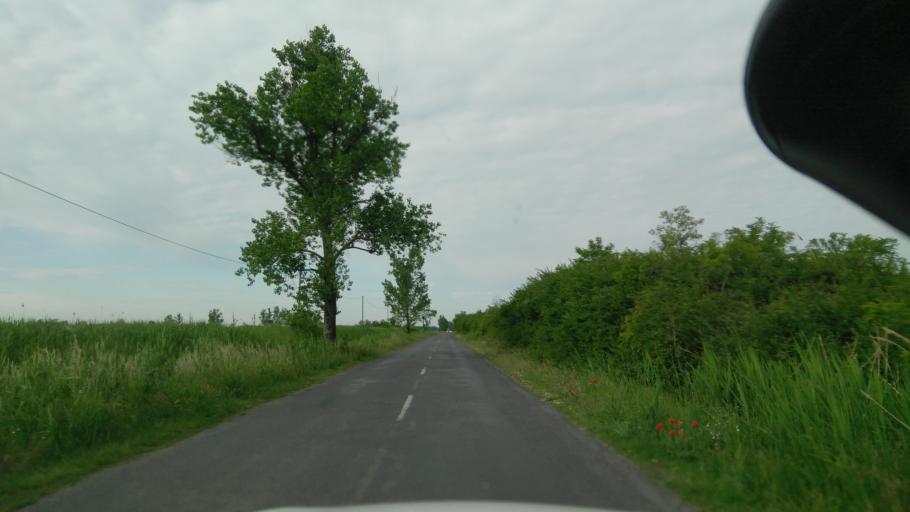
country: HU
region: Bekes
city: Elek
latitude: 46.5805
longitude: 21.2202
